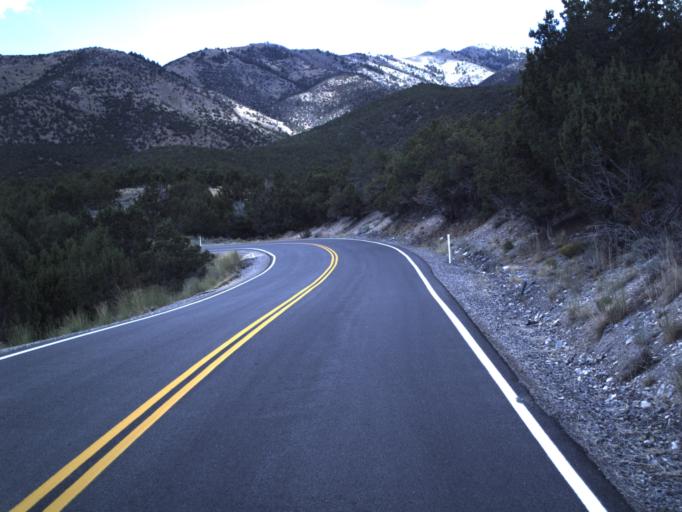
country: US
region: Utah
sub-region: Tooele County
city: Grantsville
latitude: 40.3488
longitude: -112.5569
